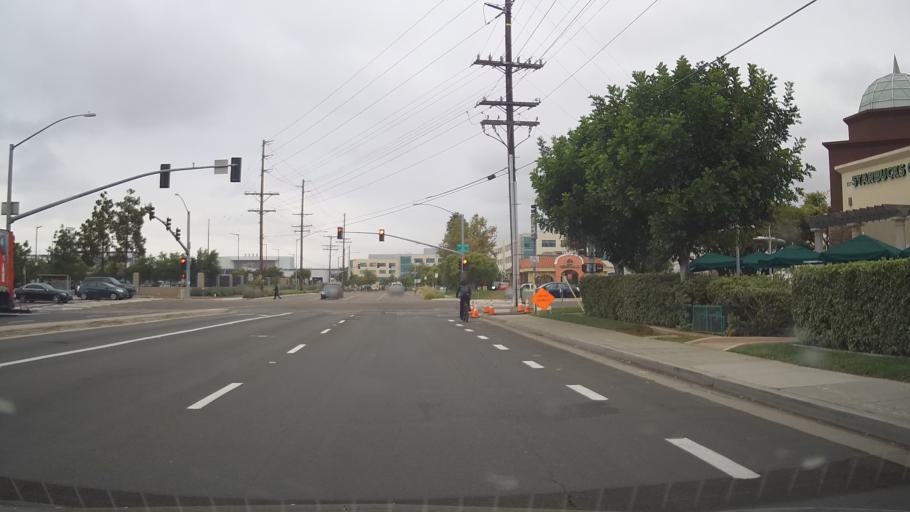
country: US
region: California
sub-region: San Diego County
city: San Diego
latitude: 32.8308
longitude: -117.1309
